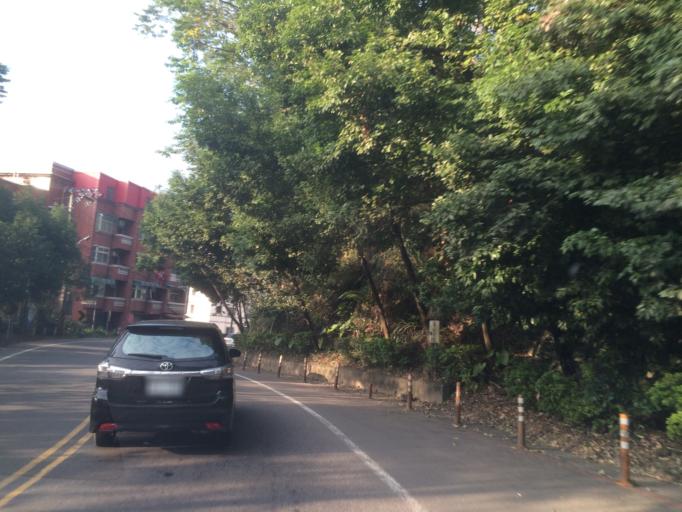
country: TW
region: Taiwan
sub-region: Hsinchu
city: Zhubei
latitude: 24.7146
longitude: 121.0981
